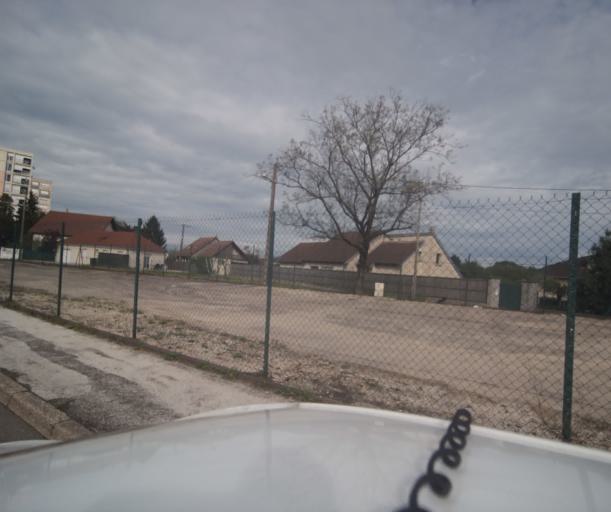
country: FR
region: Franche-Comte
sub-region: Departement du Doubs
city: Beure
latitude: 47.2311
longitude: 5.9825
